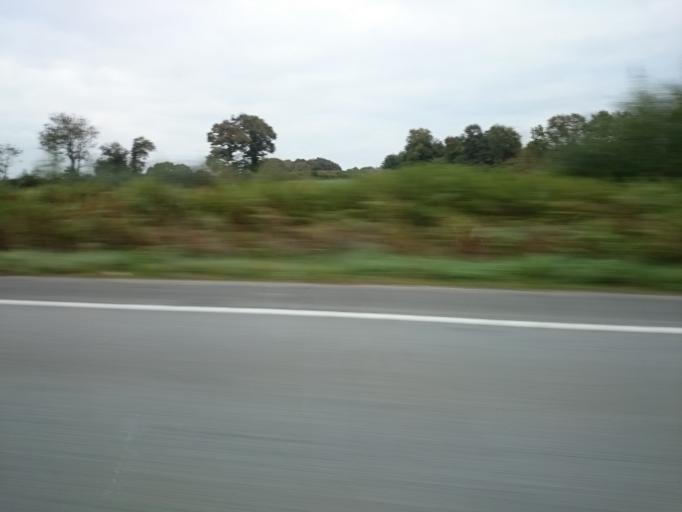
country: FR
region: Brittany
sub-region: Departement du Morbihan
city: Landaul
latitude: 47.7414
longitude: -3.0990
